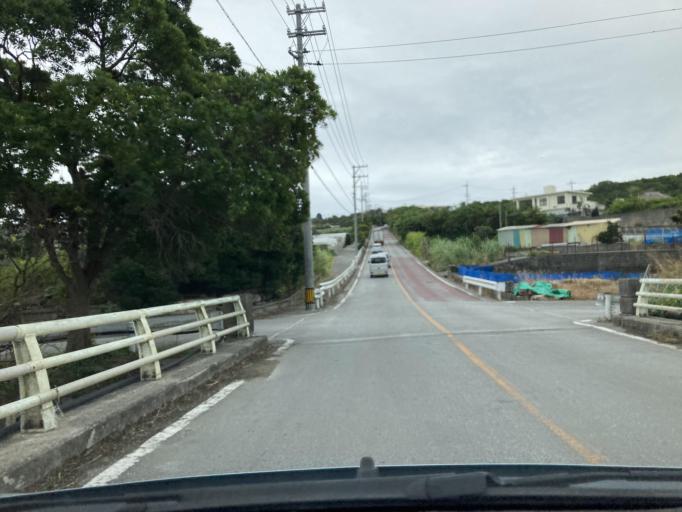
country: JP
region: Okinawa
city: Tomigusuku
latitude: 26.1677
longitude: 127.7098
